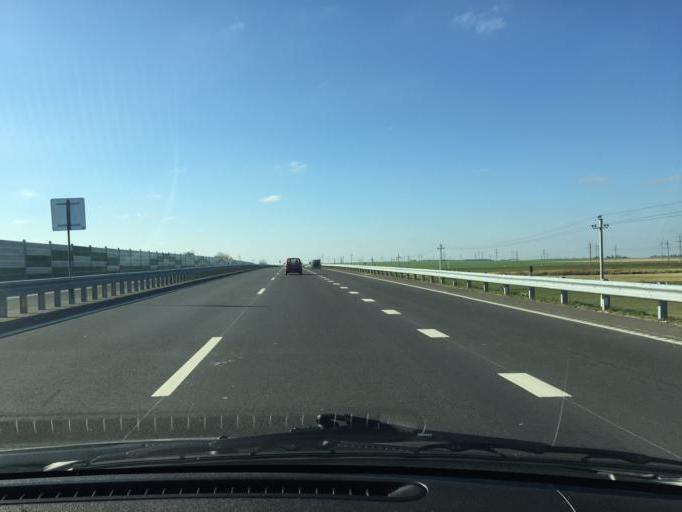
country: BY
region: Minsk
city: Slutsk
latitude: 53.0478
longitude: 27.5118
